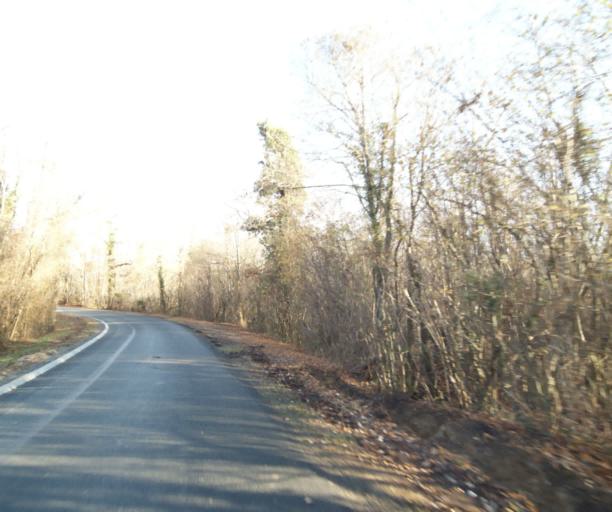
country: FR
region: Poitou-Charentes
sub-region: Departement de la Charente-Maritime
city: Cherac
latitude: 45.7174
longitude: -0.4632
